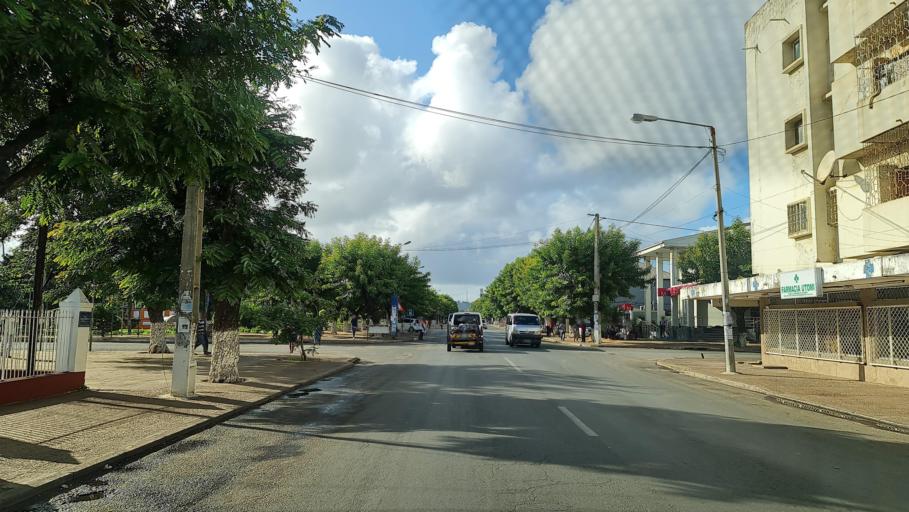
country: MZ
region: Gaza
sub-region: Xai-Xai District
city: Xai-Xai
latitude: -25.0409
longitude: 33.6405
